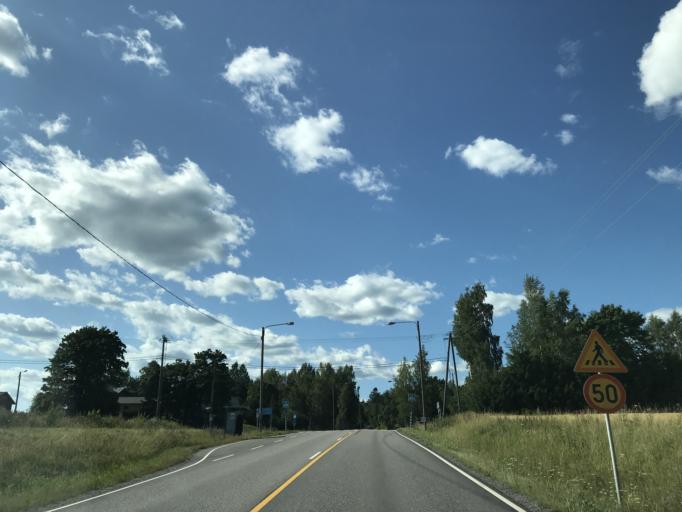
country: FI
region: Uusimaa
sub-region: Helsinki
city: Nurmijaervi
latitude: 60.4204
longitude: 24.8692
